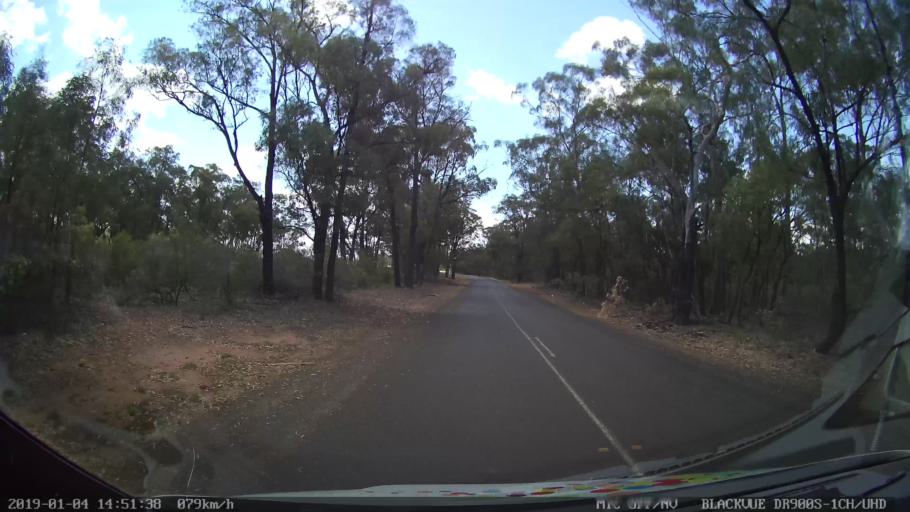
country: AU
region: New South Wales
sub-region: Dubbo Municipality
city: Dubbo
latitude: -32.0249
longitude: 148.6511
